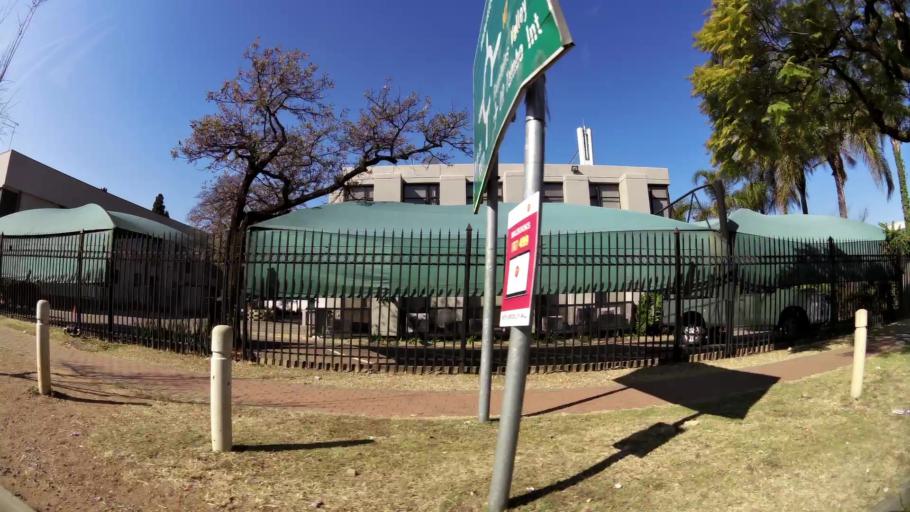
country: ZA
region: Gauteng
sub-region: City of Tshwane Metropolitan Municipality
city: Pretoria
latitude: -25.7696
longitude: 28.2354
